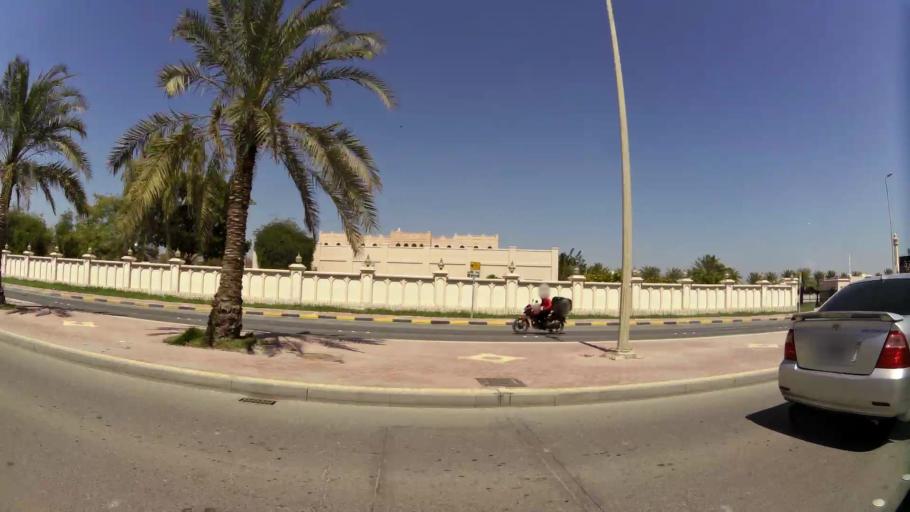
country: BH
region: Manama
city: Manama
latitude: 26.2168
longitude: 50.5930
